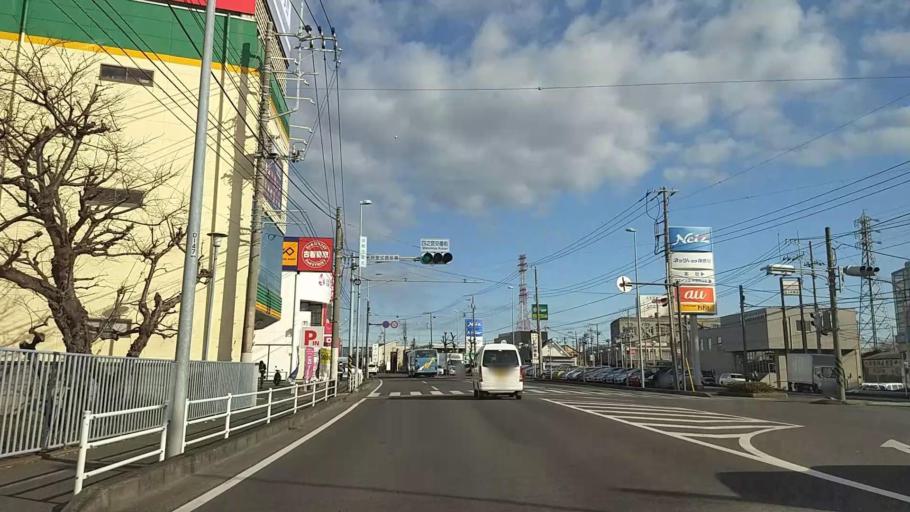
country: JP
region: Kanagawa
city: Hiratsuka
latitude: 35.3627
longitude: 139.3608
